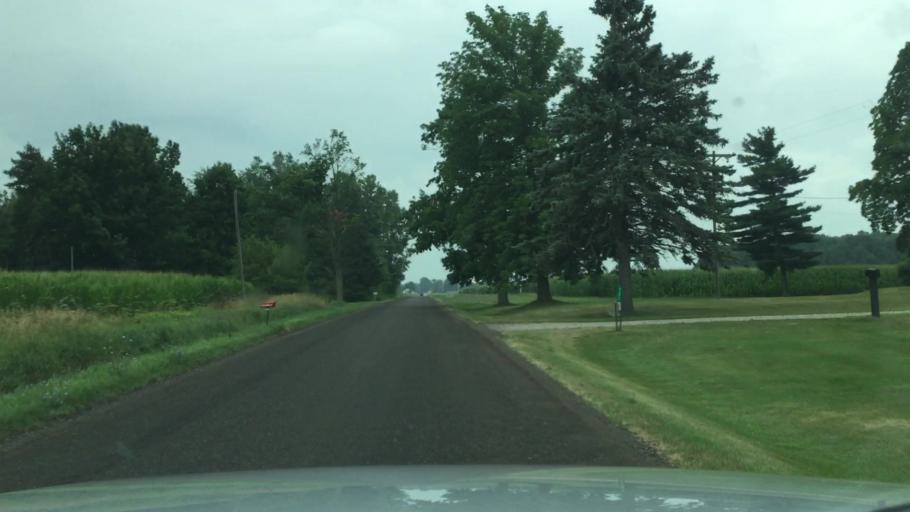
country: US
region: Michigan
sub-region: Shiawassee County
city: New Haven
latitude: 43.1053
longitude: -84.2260
